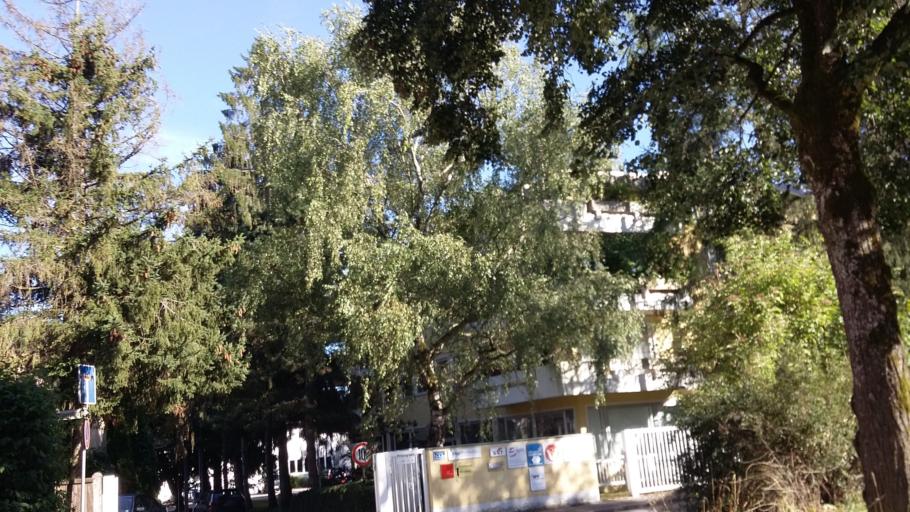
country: DE
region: Bavaria
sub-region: Upper Bavaria
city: Planegg
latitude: 48.0953
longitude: 11.4093
